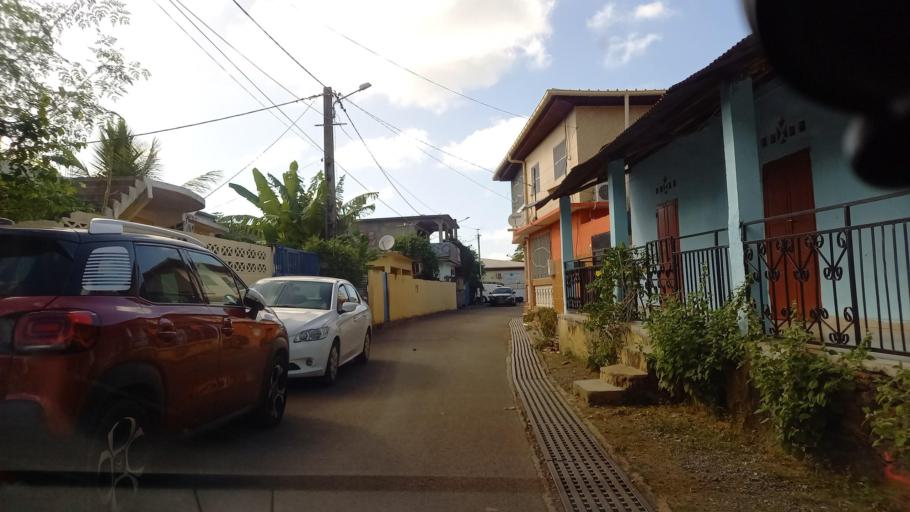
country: YT
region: Bandrele
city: Bandrele
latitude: -12.9093
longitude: 45.1951
